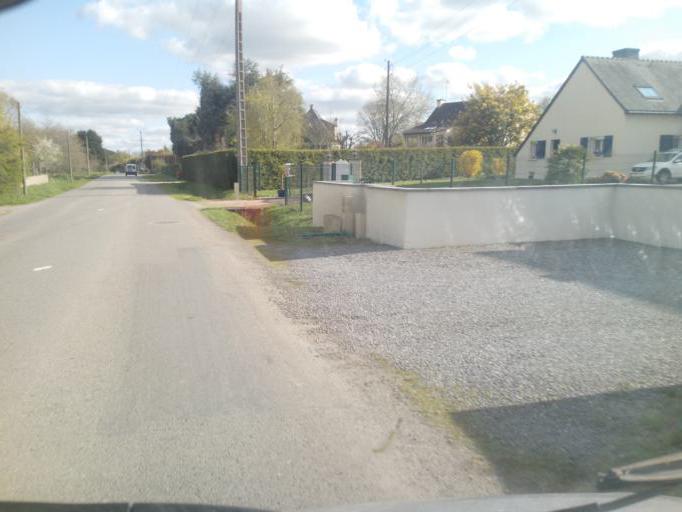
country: FR
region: Brittany
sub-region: Departement d'Ille-et-Vilaine
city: Grand-Fougeray
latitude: 47.7372
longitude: -1.7418
